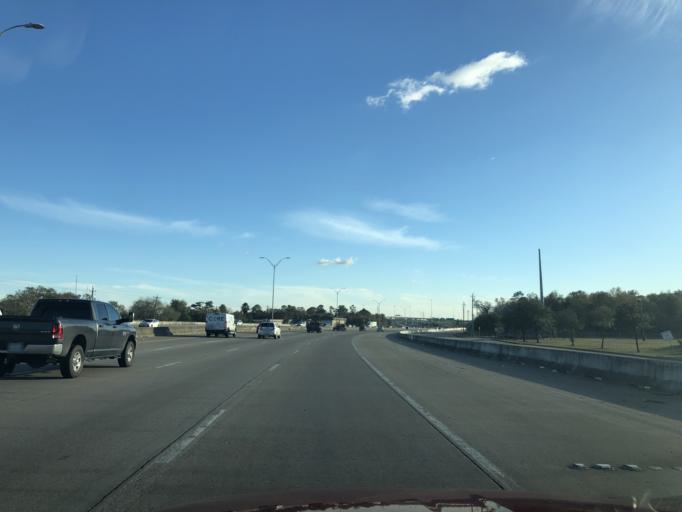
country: US
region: Texas
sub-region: Harris County
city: Cloverleaf
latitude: 29.7855
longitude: -95.1593
